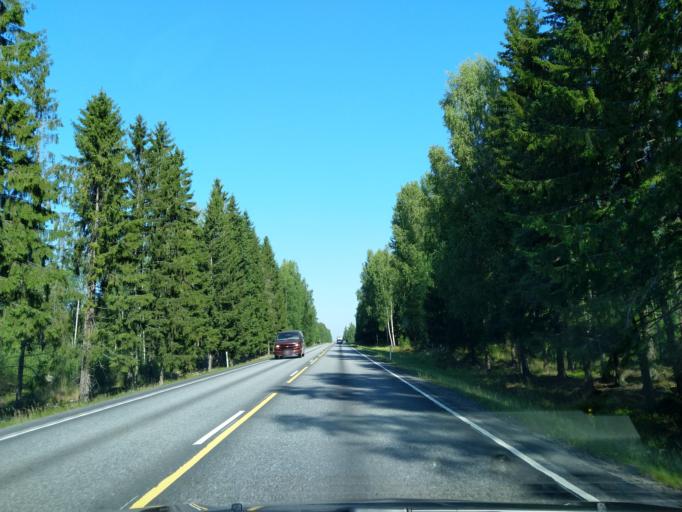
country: FI
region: Varsinais-Suomi
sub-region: Loimaa
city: Alastaro
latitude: 61.0734
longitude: 22.9166
